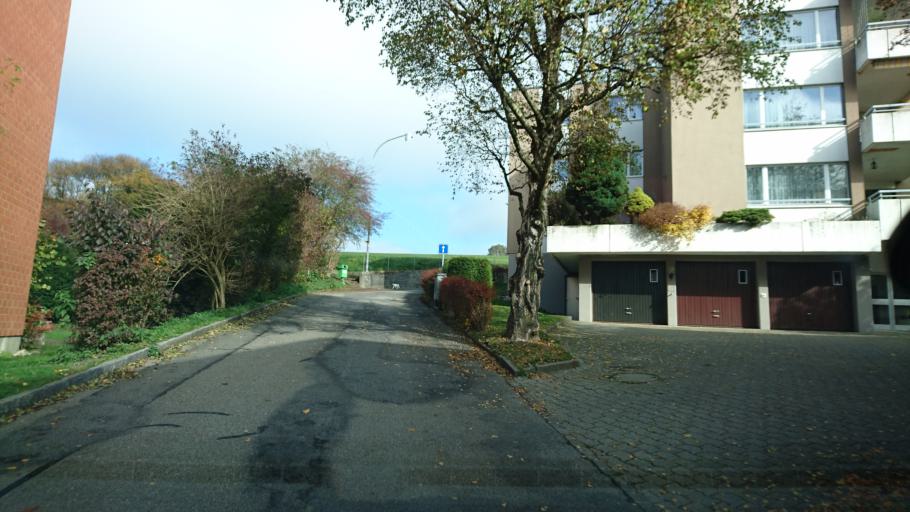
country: CH
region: Bern
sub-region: Bern-Mittelland District
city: Kirchlindach
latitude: 46.9971
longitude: 7.3959
